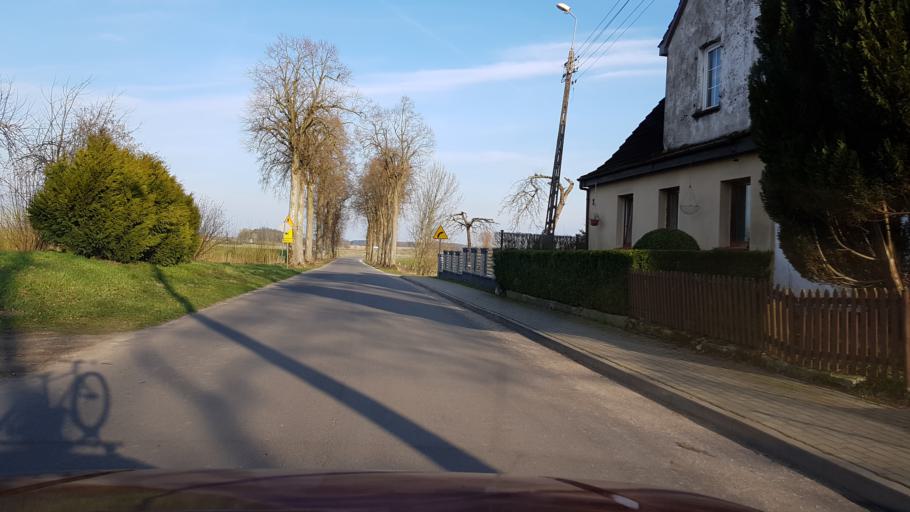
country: PL
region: West Pomeranian Voivodeship
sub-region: Powiat bialogardzki
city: Bialogard
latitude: 54.1244
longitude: 15.9954
